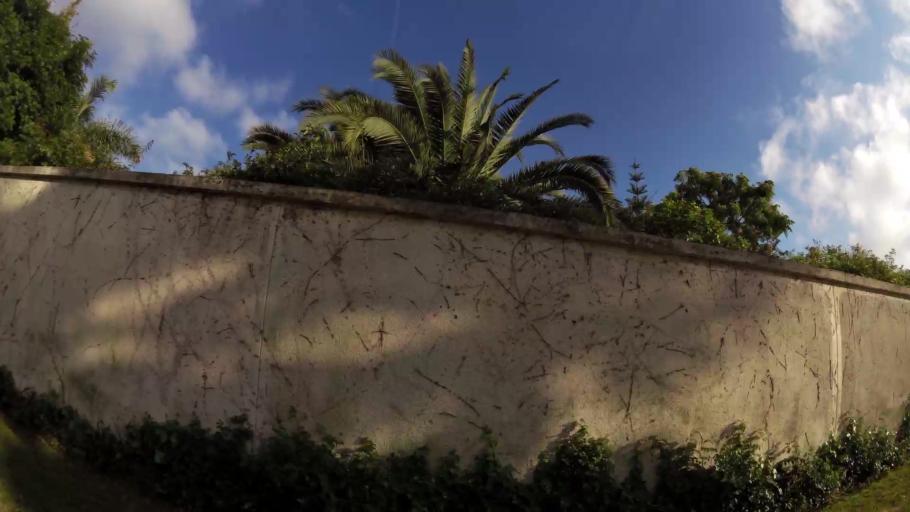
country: MA
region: Rabat-Sale-Zemmour-Zaer
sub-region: Rabat
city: Rabat
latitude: 33.9623
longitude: -6.8463
